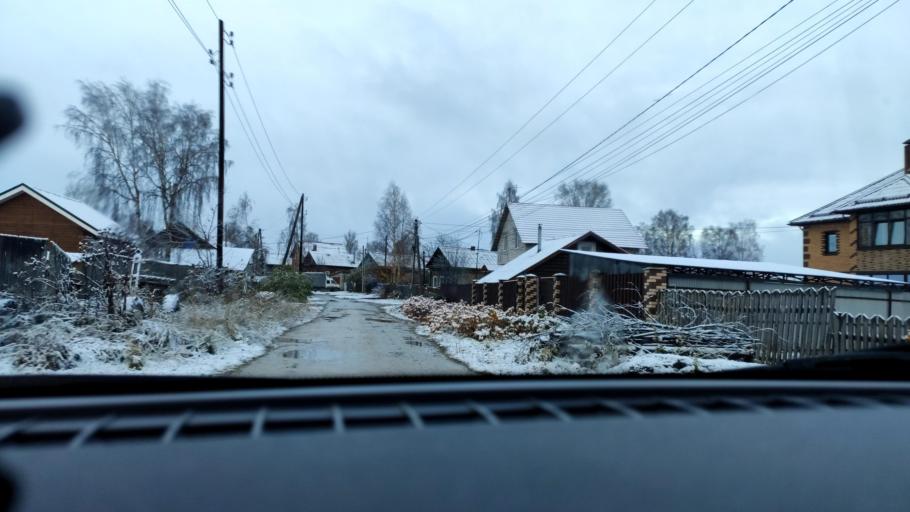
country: RU
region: Perm
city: Kondratovo
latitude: 58.0483
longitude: 56.0440
